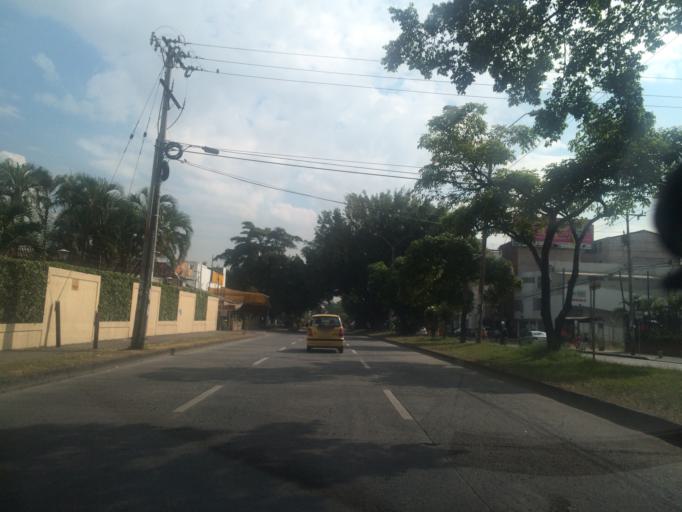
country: CO
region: Valle del Cauca
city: Cali
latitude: 3.4150
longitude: -76.5405
